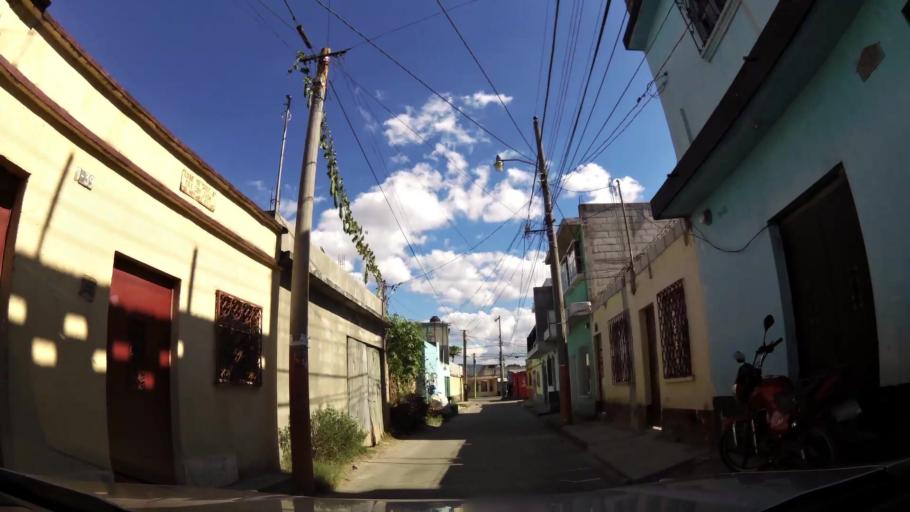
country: GT
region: Guatemala
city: Petapa
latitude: 14.5018
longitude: -90.5685
